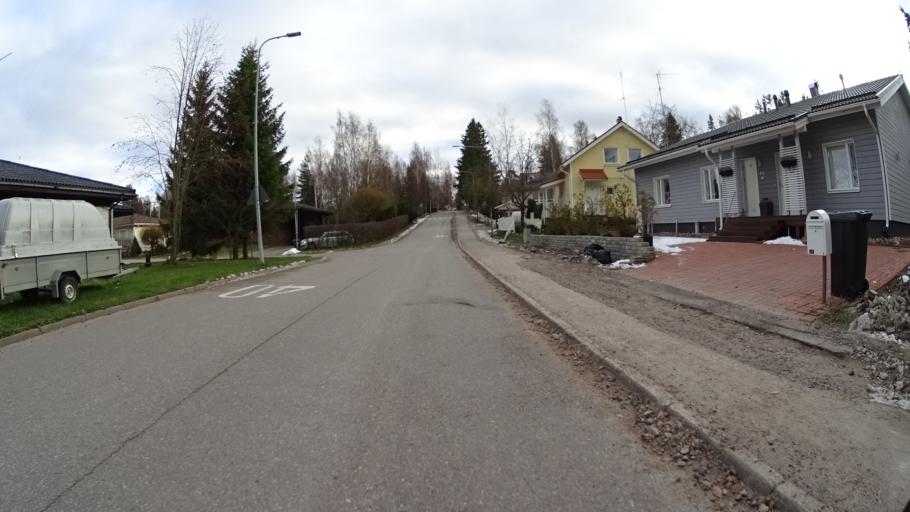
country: FI
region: Uusimaa
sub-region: Helsinki
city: Kilo
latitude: 60.2643
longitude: 24.8191
